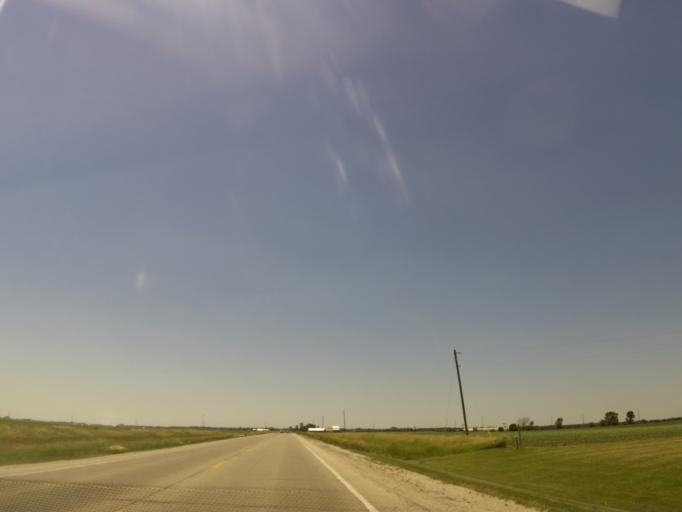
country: US
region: Illinois
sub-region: Livingston County
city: Forrest
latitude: 40.7448
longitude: -88.4596
